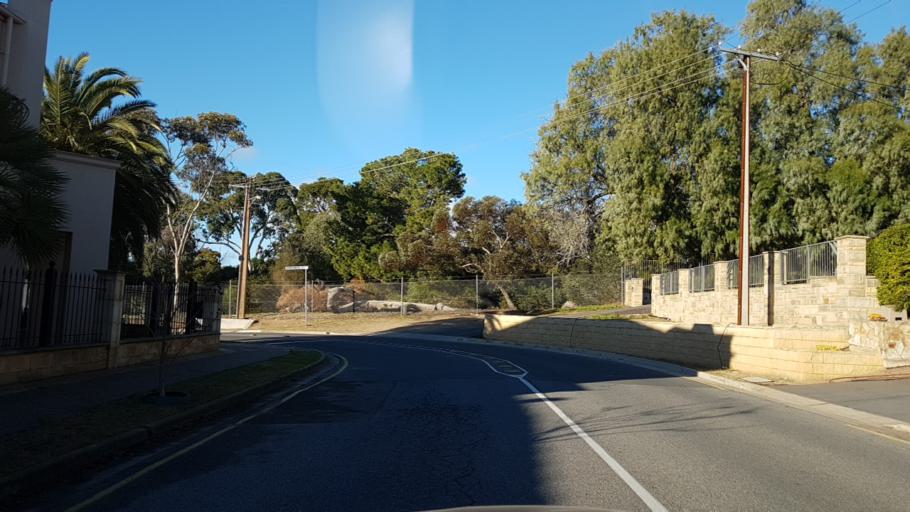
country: AU
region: South Australia
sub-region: City of West Torrens
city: Plympton
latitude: -34.9309
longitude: 138.5251
